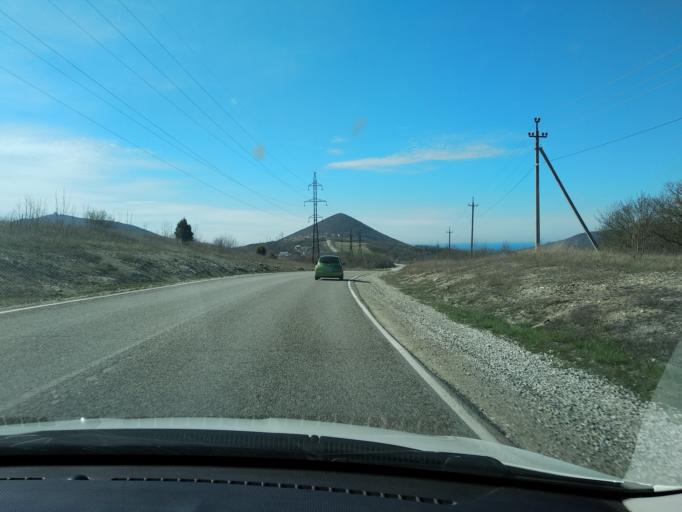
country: RU
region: Krasnodarskiy
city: Myskhako
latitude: 44.7018
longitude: 37.7172
